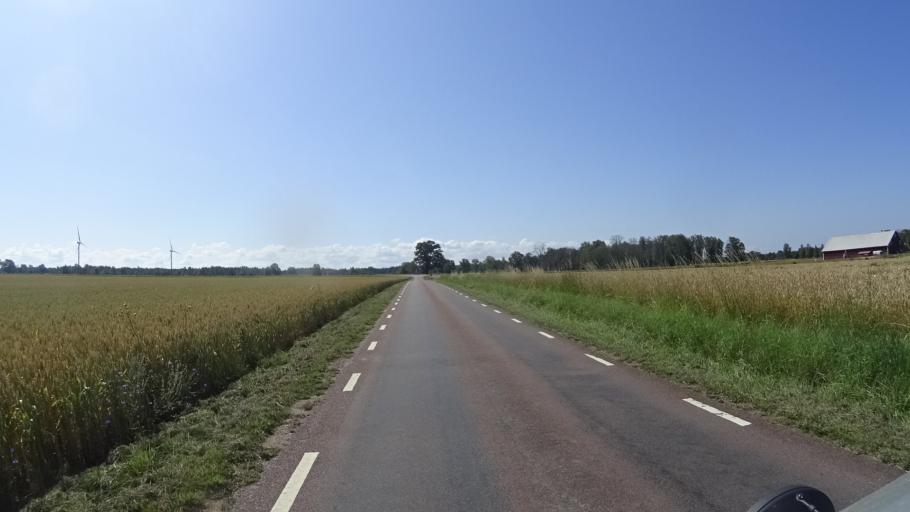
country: SE
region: OEstergoetland
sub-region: Vadstena Kommun
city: Herrestad
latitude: 58.3084
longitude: 14.8435
